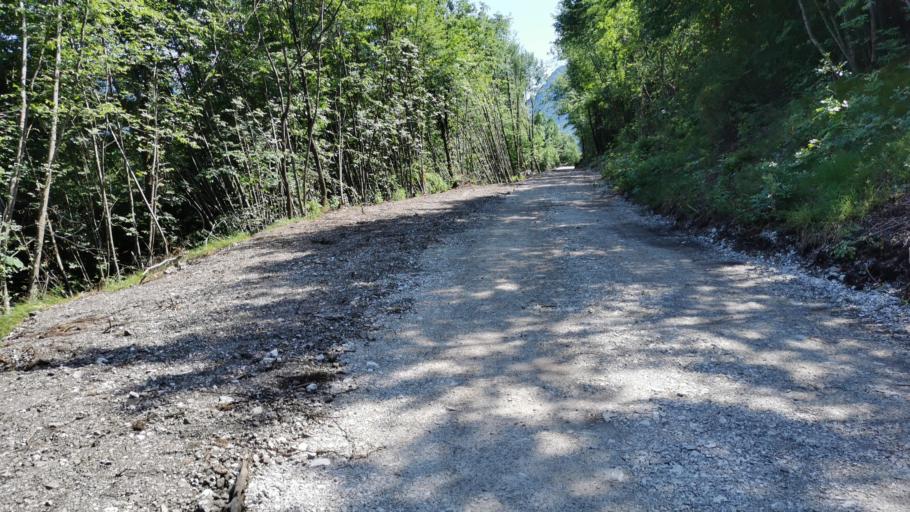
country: IT
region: Lombardy
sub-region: Provincia di Brescia
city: Ponte Caffaro
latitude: 45.8021
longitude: 10.5072
